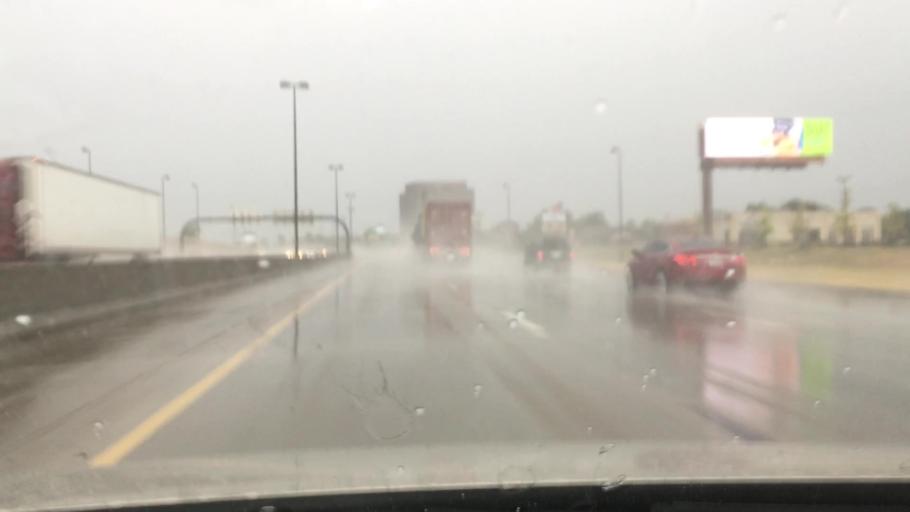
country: US
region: Oklahoma
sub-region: Tulsa County
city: Jenks
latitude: 36.0907
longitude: -95.9358
